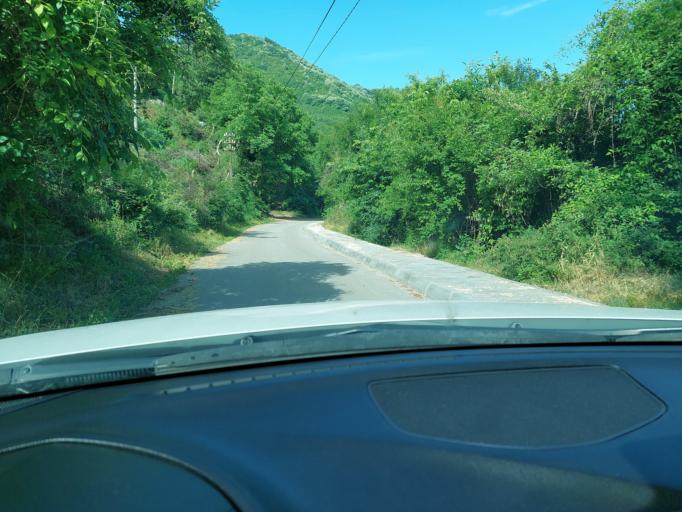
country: MK
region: Kratovo
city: Kratovo
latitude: 42.0793
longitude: 22.1683
